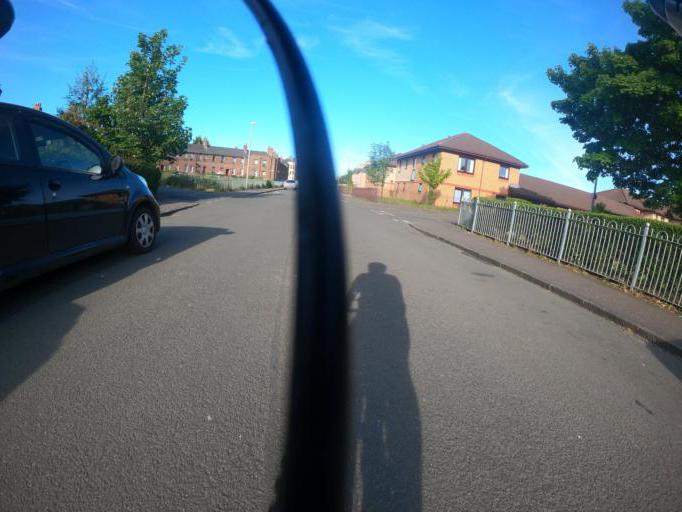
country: GB
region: Scotland
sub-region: Edinburgh
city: Edinburgh
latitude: 55.9771
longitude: -3.2359
